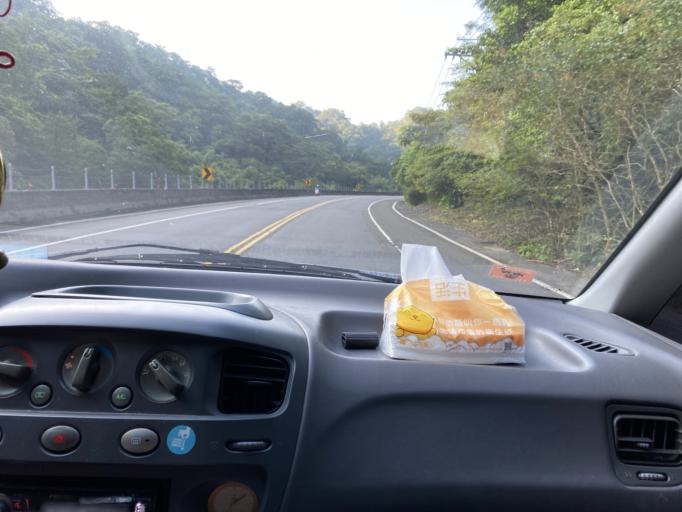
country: TW
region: Taiwan
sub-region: Keelung
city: Keelung
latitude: 25.0359
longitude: 121.7793
